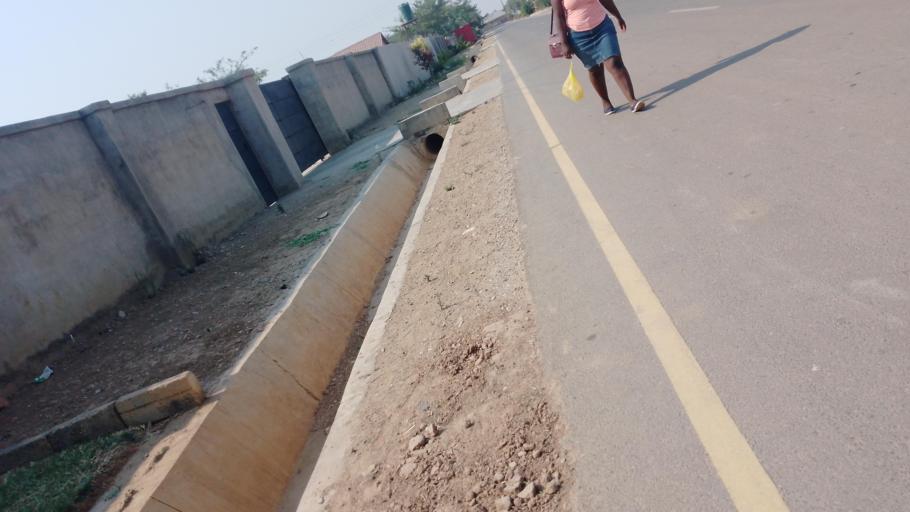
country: ZM
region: Lusaka
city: Lusaka
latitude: -15.3886
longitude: 28.3914
